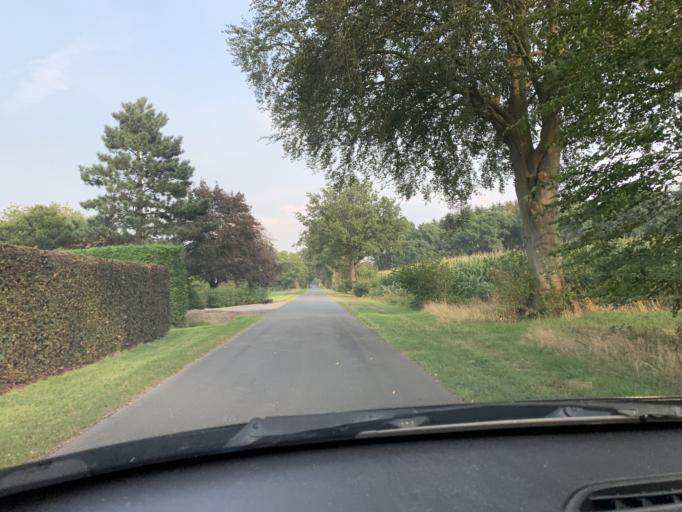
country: DE
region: Lower Saxony
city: Westerstede
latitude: 53.2584
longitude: 7.8858
